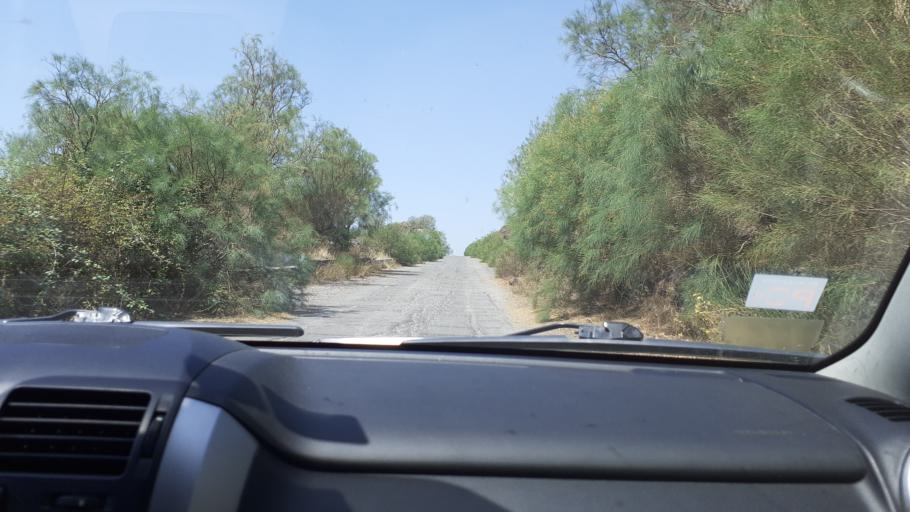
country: IT
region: Sicily
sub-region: Catania
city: Nicolosi
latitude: 37.6467
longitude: 15.0112
